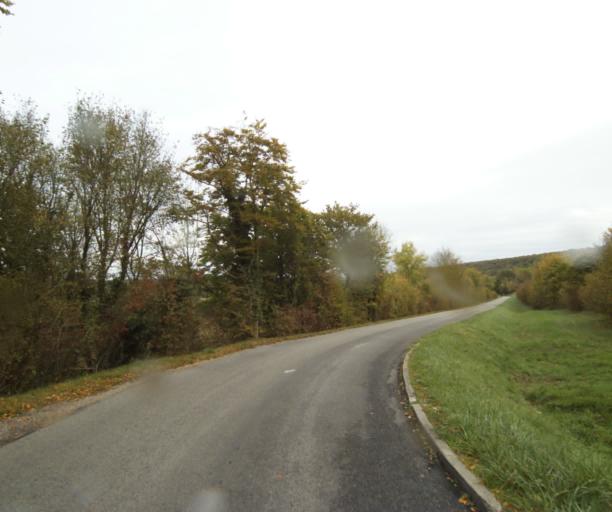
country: FR
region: Centre
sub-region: Departement d'Eure-et-Loir
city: Vert-en-Drouais
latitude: 48.7584
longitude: 1.3243
